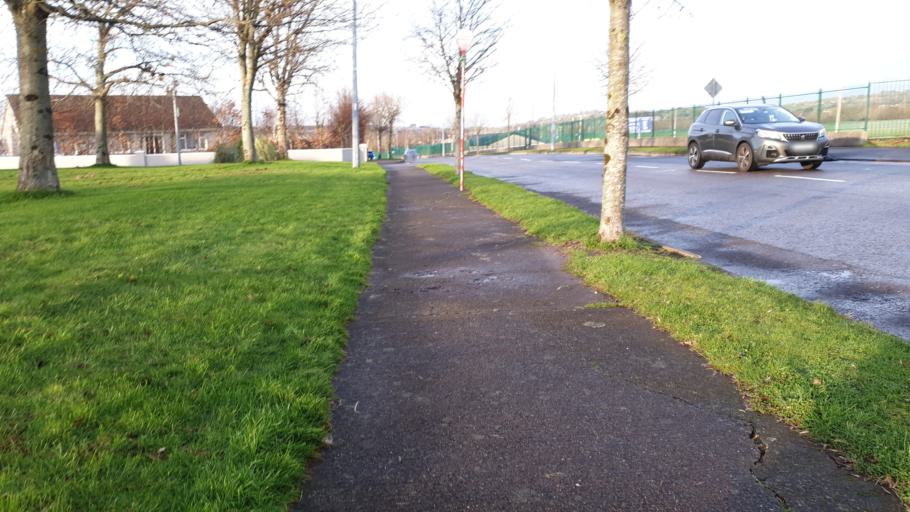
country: IE
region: Munster
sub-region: County Cork
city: Passage West
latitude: 51.8882
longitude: -8.3940
